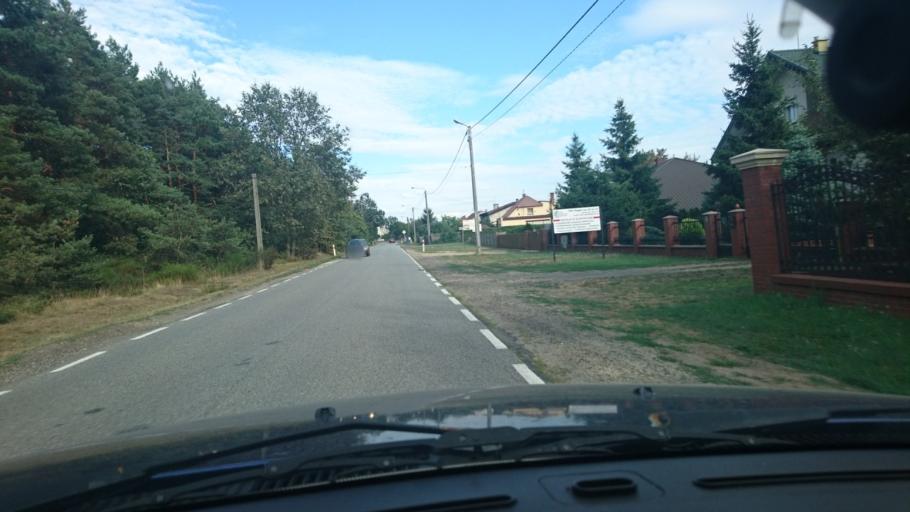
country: PL
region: Greater Poland Voivodeship
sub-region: Powiat ostrzeszowski
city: Ostrzeszow
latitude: 51.4314
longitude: 17.9096
